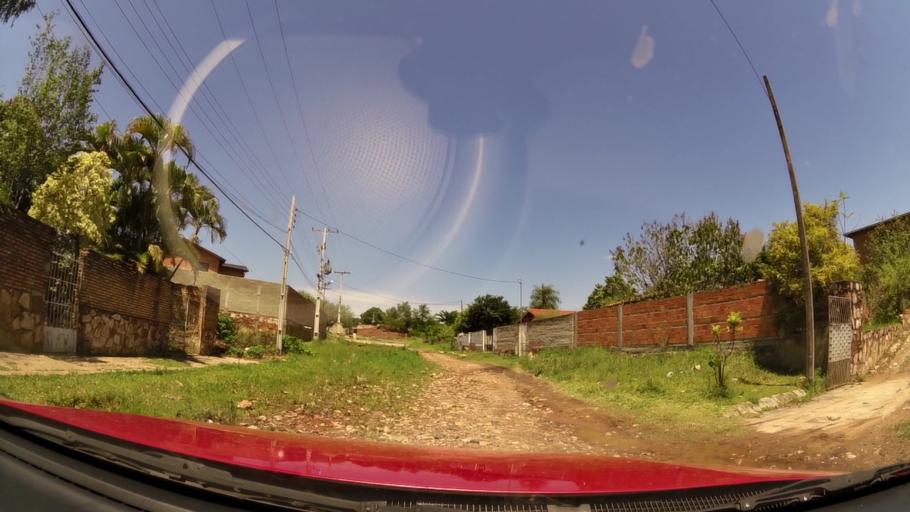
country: PY
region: Central
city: Colonia Mariano Roque Alonso
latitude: -25.2377
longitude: -57.5471
